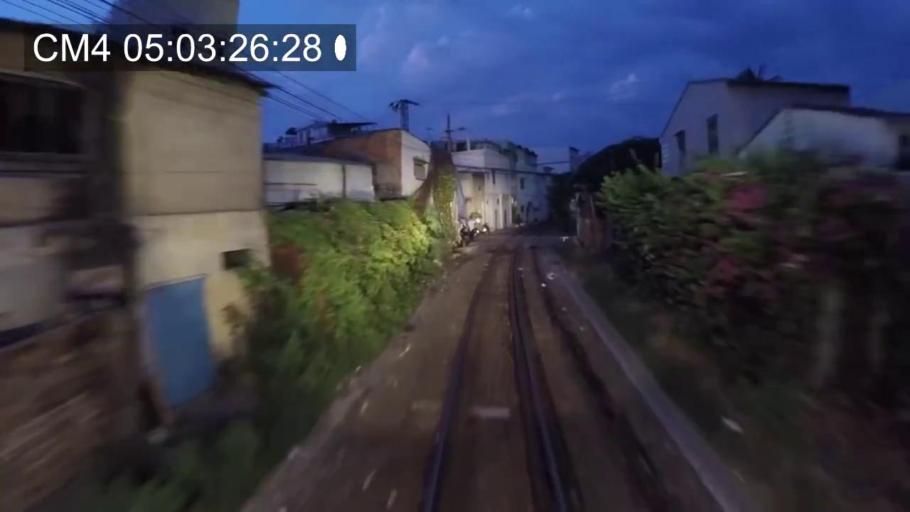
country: VN
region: Khanh Hoa
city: Nha Trang
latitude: 12.2560
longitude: 109.1709
